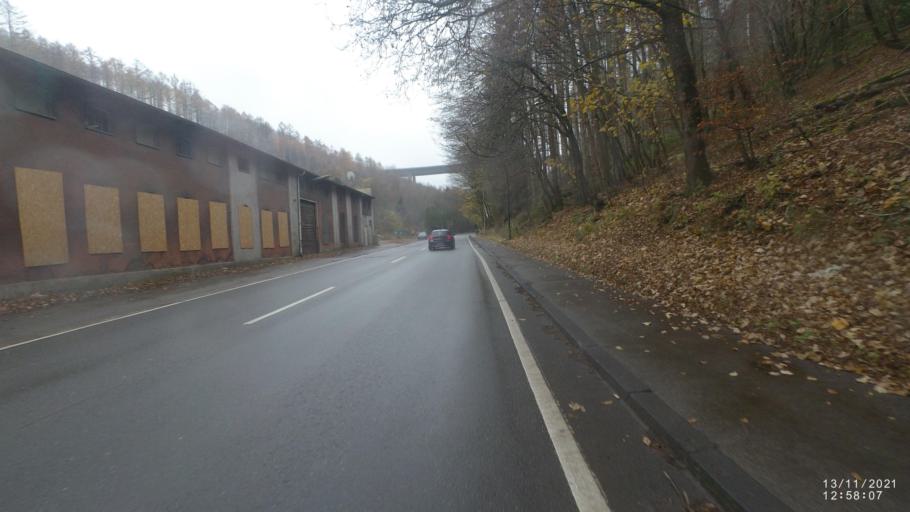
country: DE
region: North Rhine-Westphalia
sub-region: Regierungsbezirk Arnsberg
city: Luedenscheid
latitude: 51.2525
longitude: 7.6264
